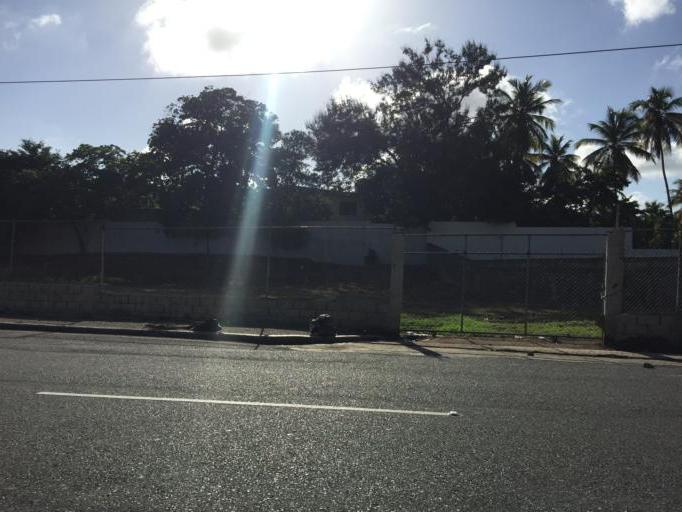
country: DO
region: Nacional
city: La Agustina
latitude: 18.4854
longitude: -69.9414
